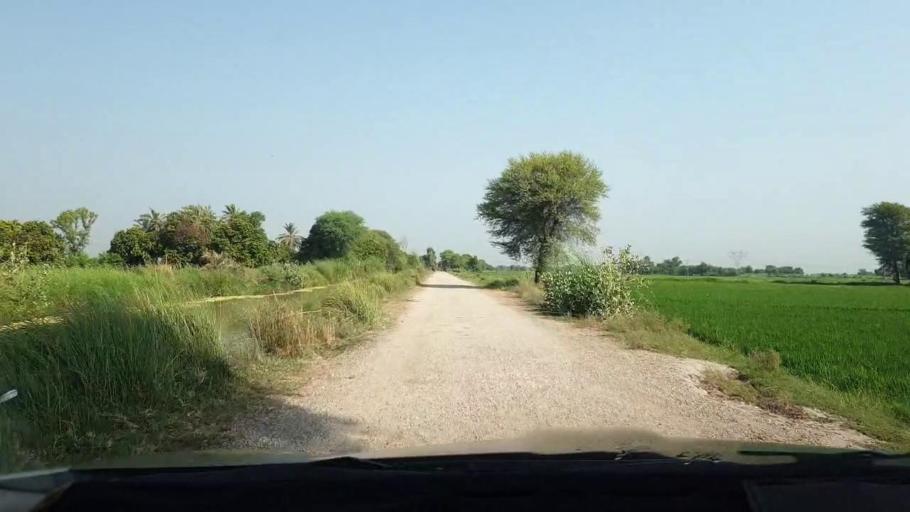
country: PK
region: Sindh
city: Larkana
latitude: 27.6333
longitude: 68.2376
